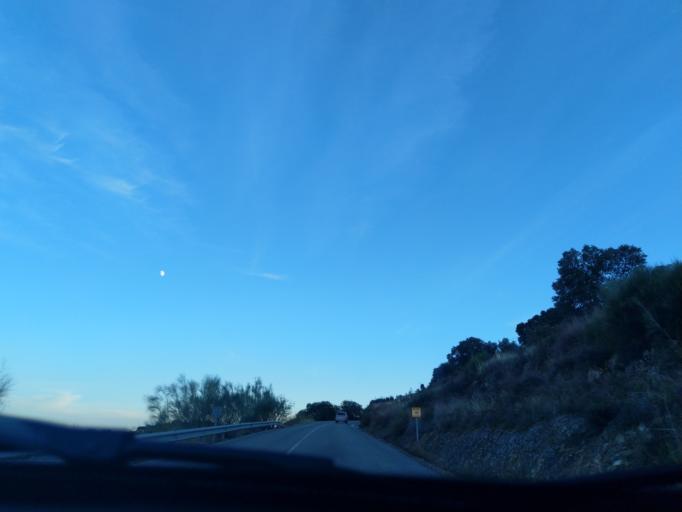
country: ES
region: Extremadura
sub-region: Provincia de Badajoz
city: Reina
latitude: 38.1590
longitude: -5.8988
